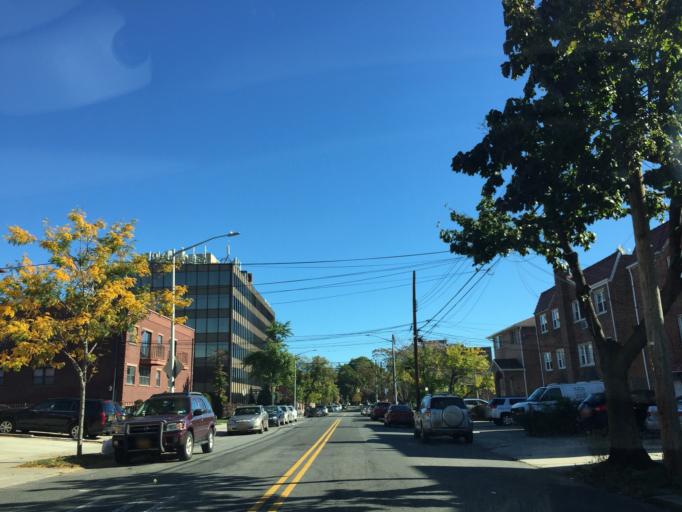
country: US
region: New York
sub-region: Nassau County
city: East Atlantic Beach
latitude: 40.7610
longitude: -73.7716
